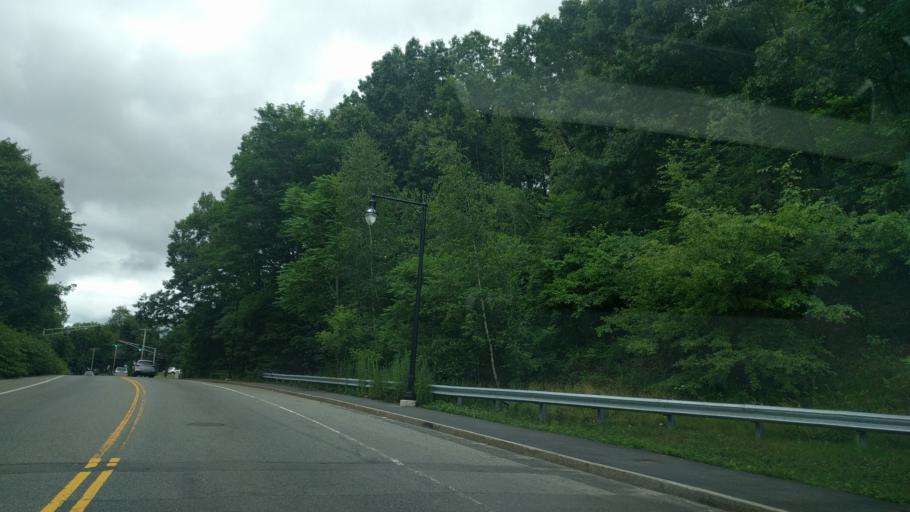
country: US
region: Massachusetts
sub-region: Worcester County
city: Worcester
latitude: 42.2377
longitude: -71.8025
